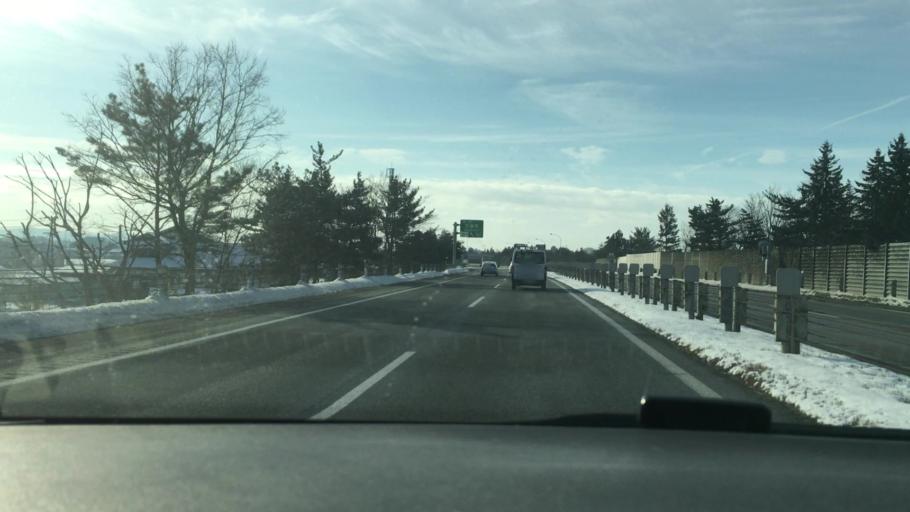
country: JP
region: Iwate
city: Hanamaki
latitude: 39.3911
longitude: 141.0918
